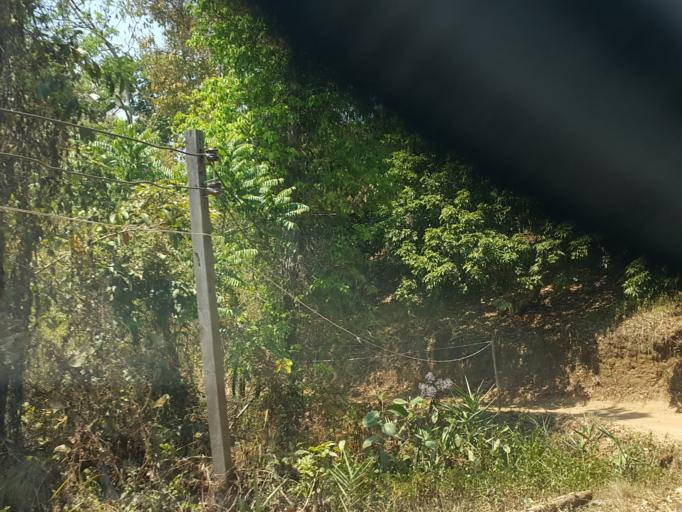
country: TH
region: Chiang Mai
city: Samoeng
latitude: 18.8874
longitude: 98.7820
